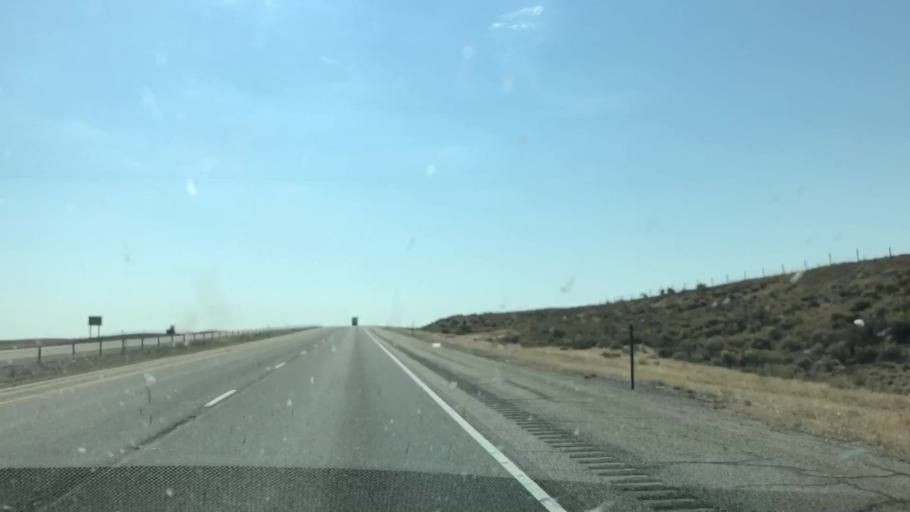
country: US
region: Wyoming
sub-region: Sweetwater County
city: Rock Springs
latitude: 41.6590
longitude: -108.7170
